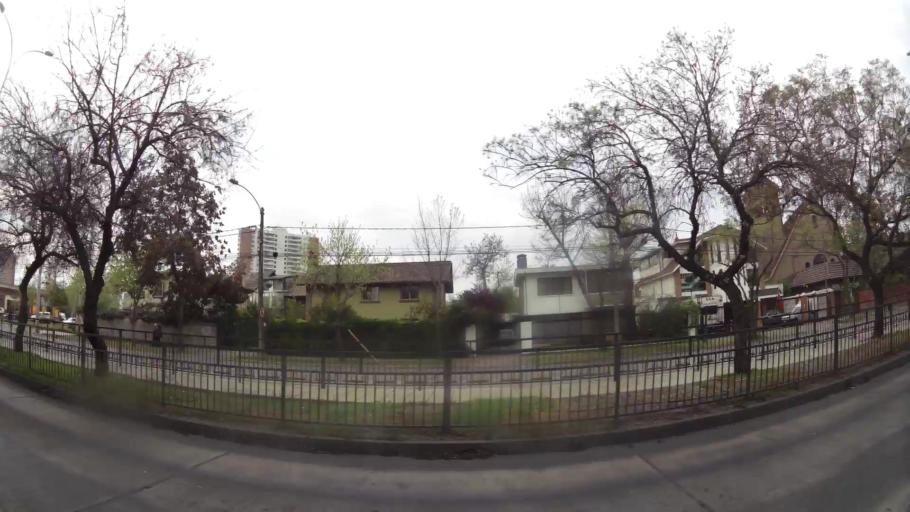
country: CL
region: Santiago Metropolitan
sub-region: Provincia de Santiago
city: Santiago
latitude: -33.4578
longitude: -70.6244
